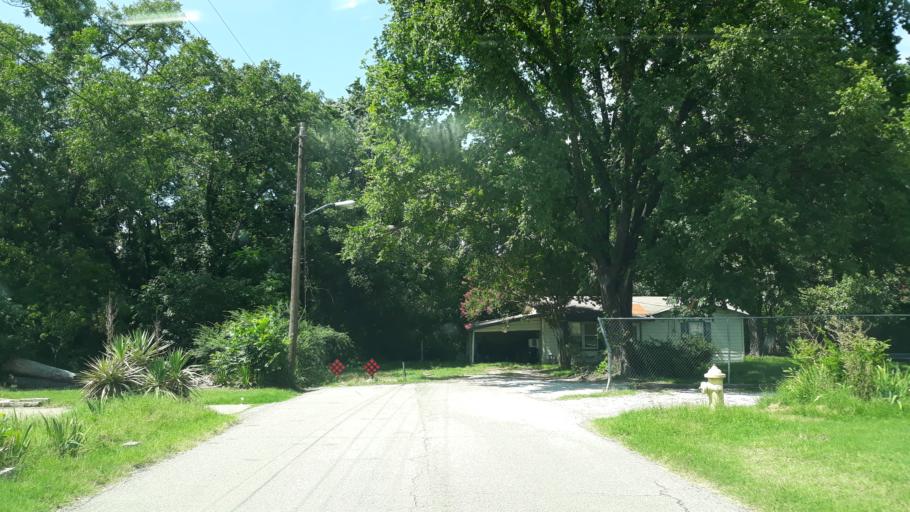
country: US
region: Texas
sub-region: Dallas County
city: Coppell
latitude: 32.9553
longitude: -97.0053
